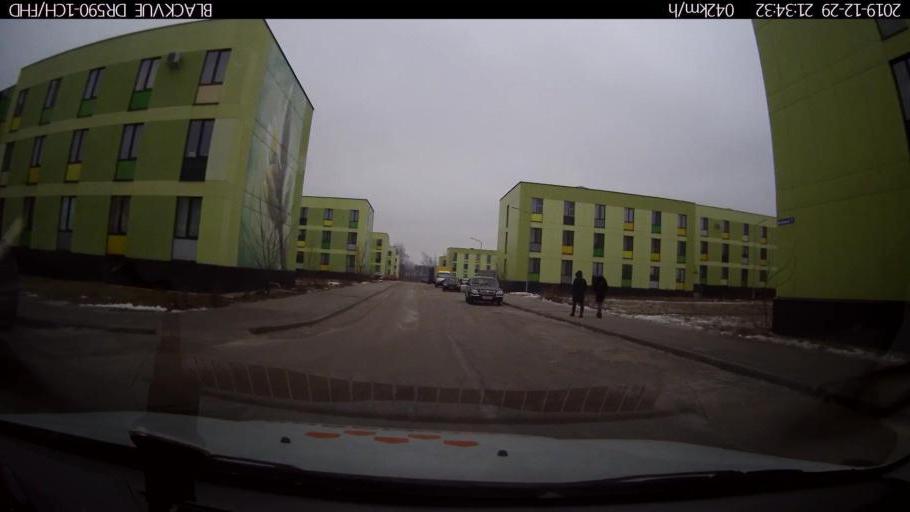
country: RU
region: Nizjnij Novgorod
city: Afonino
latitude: 56.2156
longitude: 44.0184
